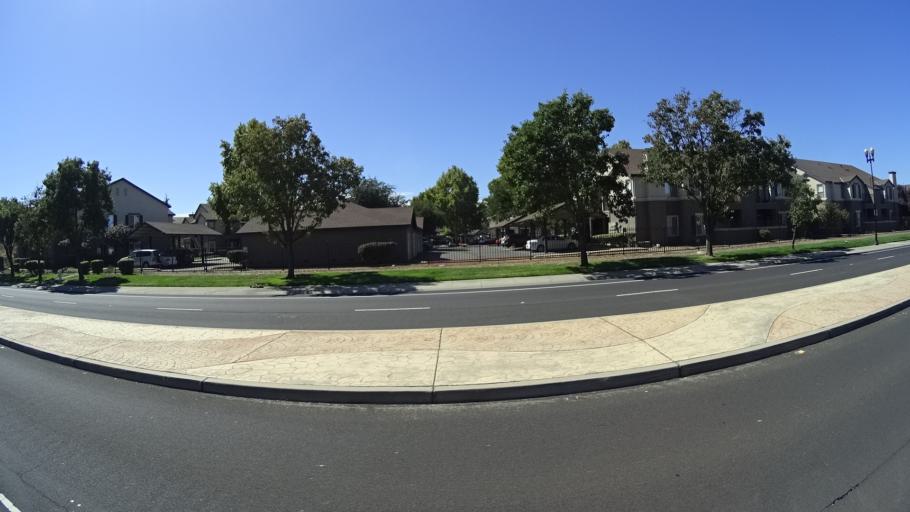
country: US
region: California
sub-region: Sacramento County
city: Laguna
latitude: 38.4129
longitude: -121.4781
